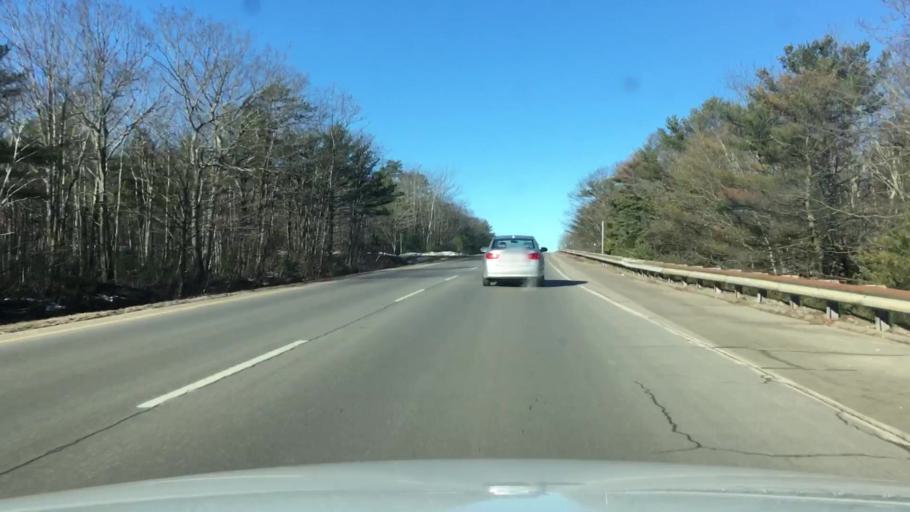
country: US
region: Maine
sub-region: Sagadahoc County
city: Bath
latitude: 43.9093
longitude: -69.8398
